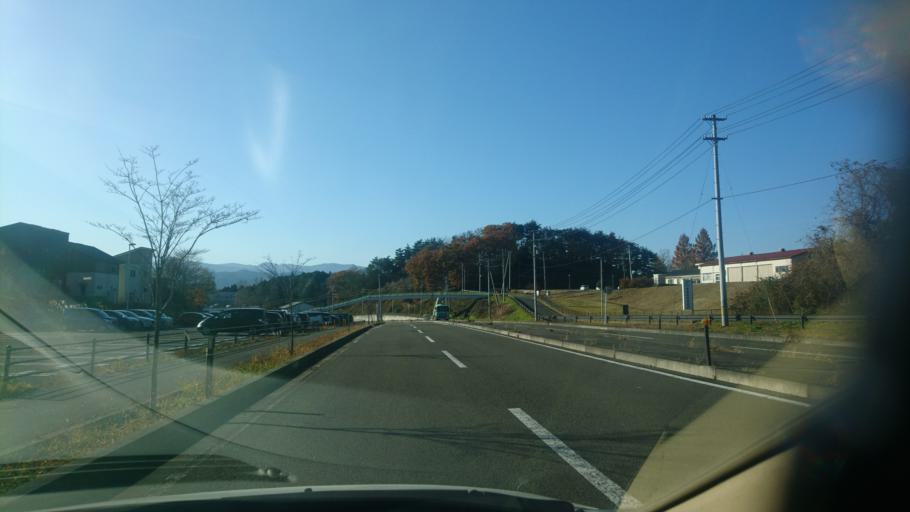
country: JP
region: Miyagi
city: Tomiya
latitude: 38.4679
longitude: 140.8832
